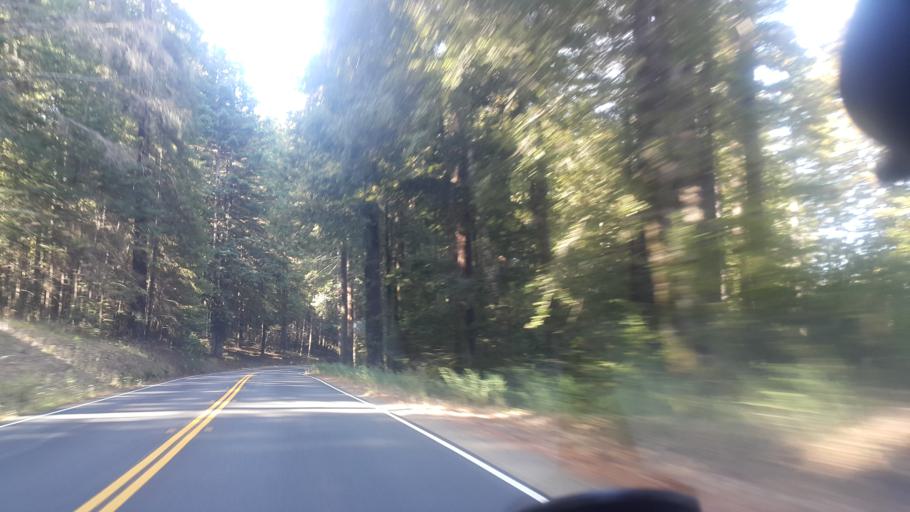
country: US
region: California
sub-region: Mendocino County
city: Fort Bragg
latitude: 39.3585
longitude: -123.6486
